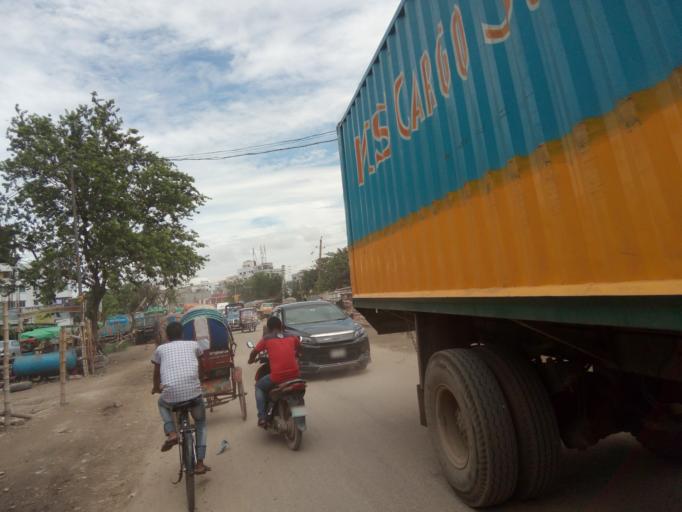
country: BD
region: Dhaka
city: Azimpur
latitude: 23.7573
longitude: 90.3555
